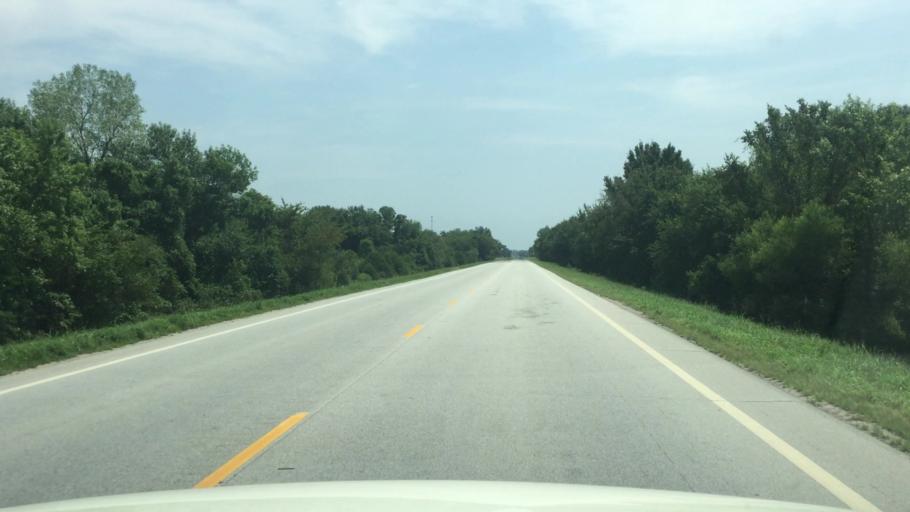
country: US
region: Kansas
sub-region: Cherokee County
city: Columbus
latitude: 37.1788
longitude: -94.8753
